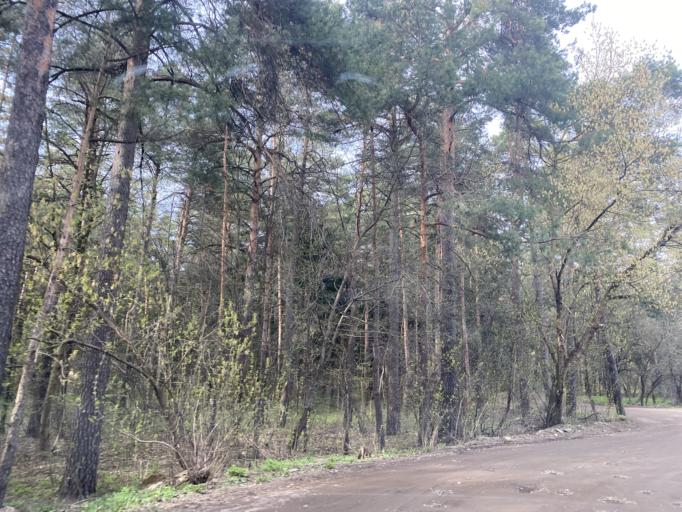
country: BY
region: Minsk
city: Vyaliki Trastsyanets
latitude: 53.9156
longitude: 27.6624
